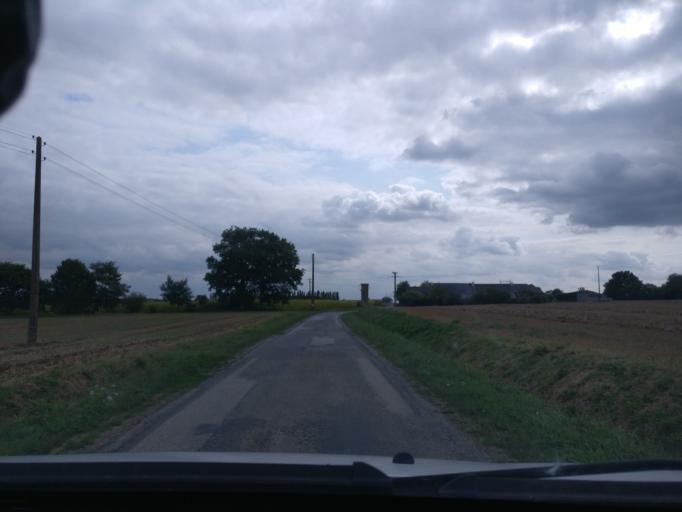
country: FR
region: Brittany
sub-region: Departement d'Ille-et-Vilaine
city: Nouvoitou
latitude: 48.0741
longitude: -1.5347
